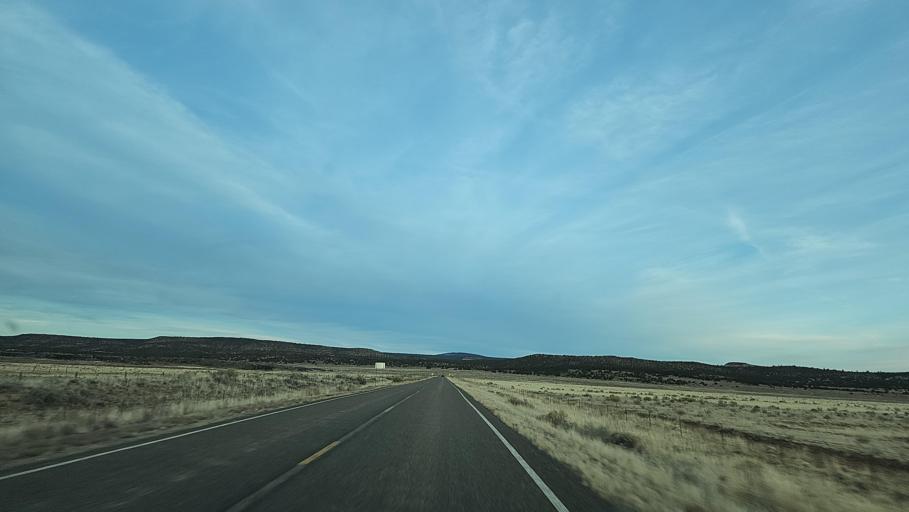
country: US
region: New Mexico
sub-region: Cibola County
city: Grants
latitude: 34.7095
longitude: -107.9993
